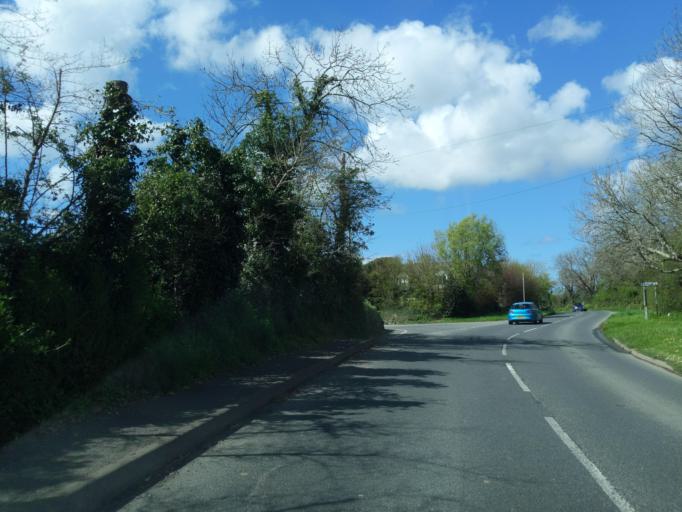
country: GB
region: England
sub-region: Cornwall
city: Wadebridge
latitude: 50.5250
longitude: -4.8311
